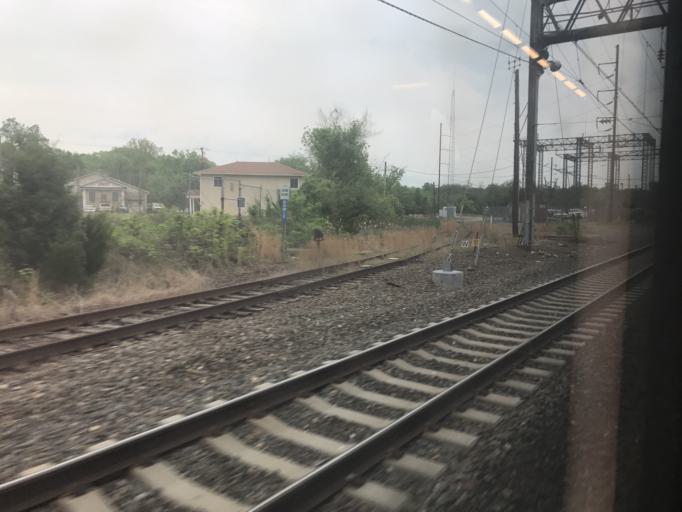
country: US
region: Maryland
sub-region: Prince George's County
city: Glenn Dale
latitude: 39.0075
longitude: -76.7795
